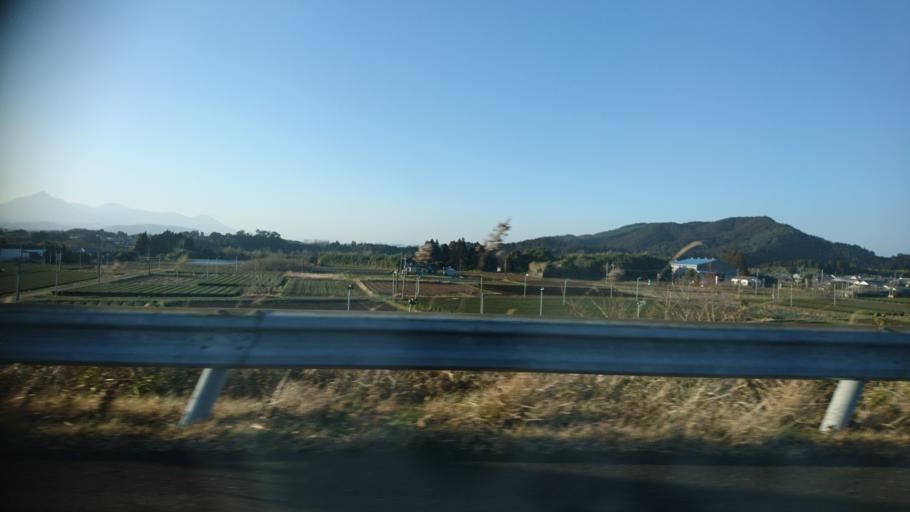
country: JP
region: Miyazaki
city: Miyakonojo
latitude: 31.7930
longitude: 131.1573
